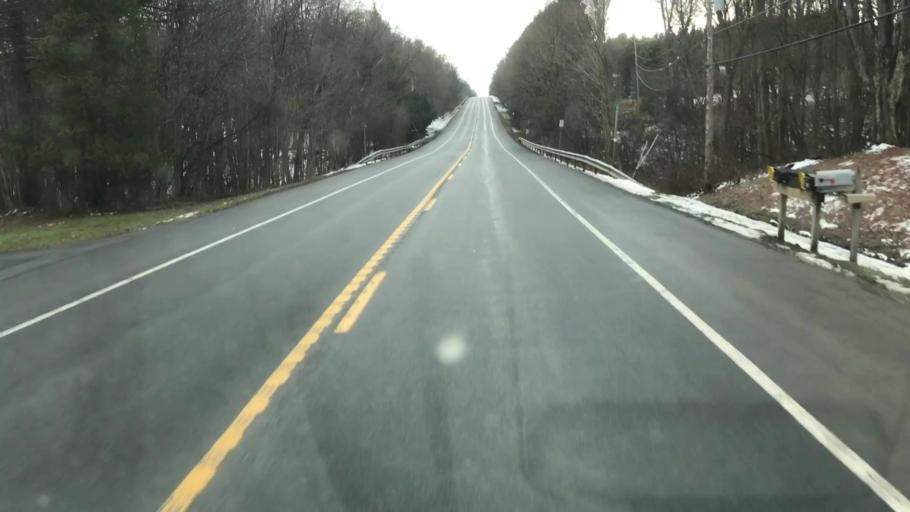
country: US
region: New York
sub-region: Onondaga County
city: Skaneateles
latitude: 42.9102
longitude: -76.4277
